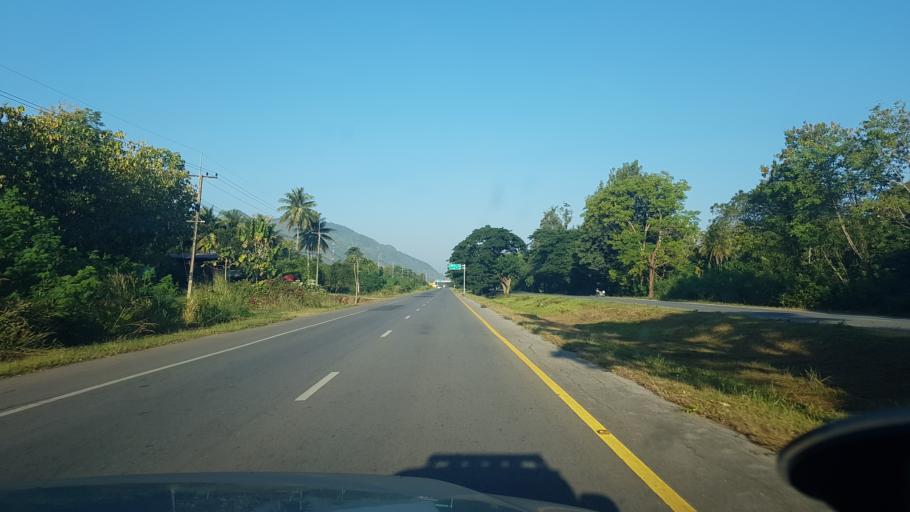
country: TH
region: Chaiyaphum
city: Khon San
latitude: 16.5985
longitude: 101.9072
